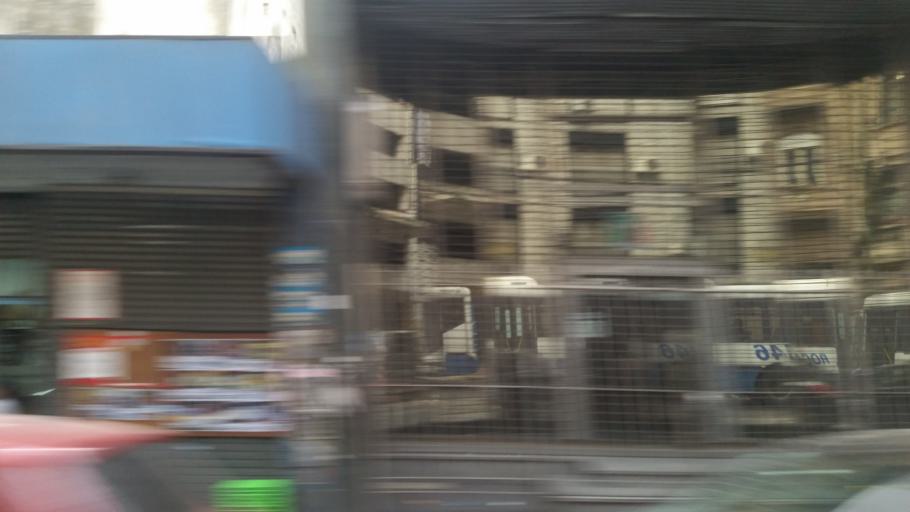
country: AR
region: Buenos Aires F.D.
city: Buenos Aires
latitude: -34.6056
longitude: -58.3948
